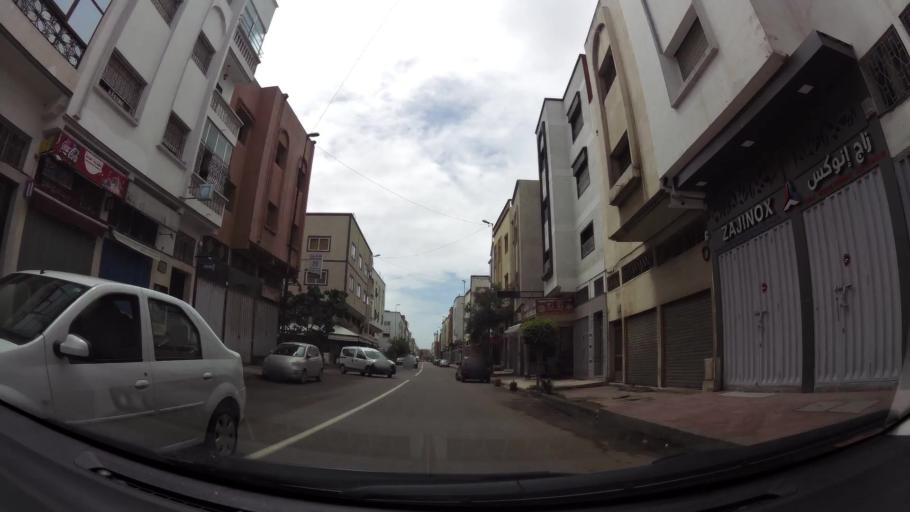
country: MA
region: Grand Casablanca
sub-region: Casablanca
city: Casablanca
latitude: 33.5417
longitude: -7.6782
